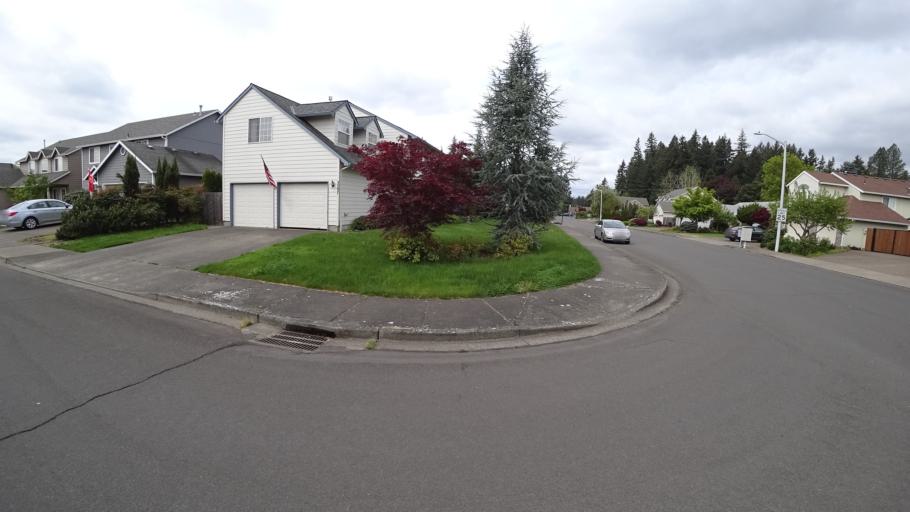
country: US
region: Oregon
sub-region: Washington County
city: Hillsboro
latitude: 45.5486
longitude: -122.9937
